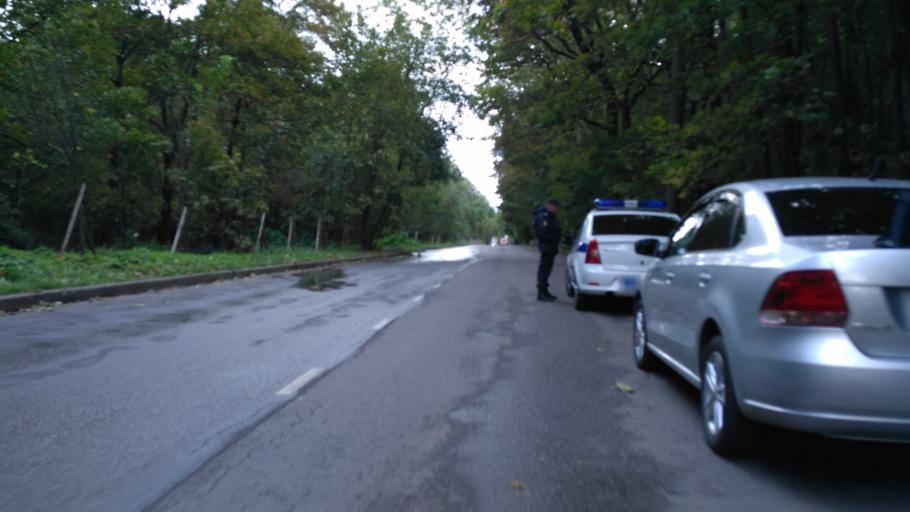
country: RU
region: Moscow
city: Sokol'niki
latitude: 55.8068
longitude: 37.6600
